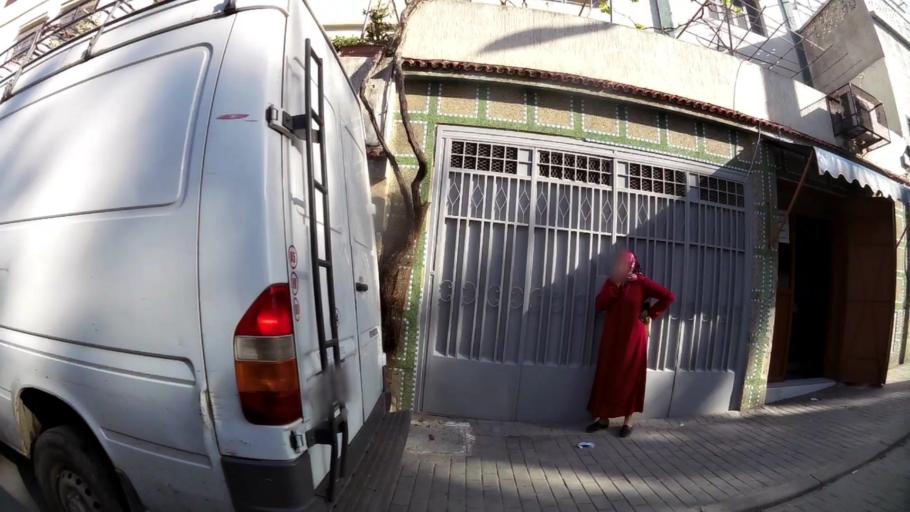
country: MA
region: Tanger-Tetouan
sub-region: Tanger-Assilah
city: Tangier
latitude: 35.7618
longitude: -5.7919
